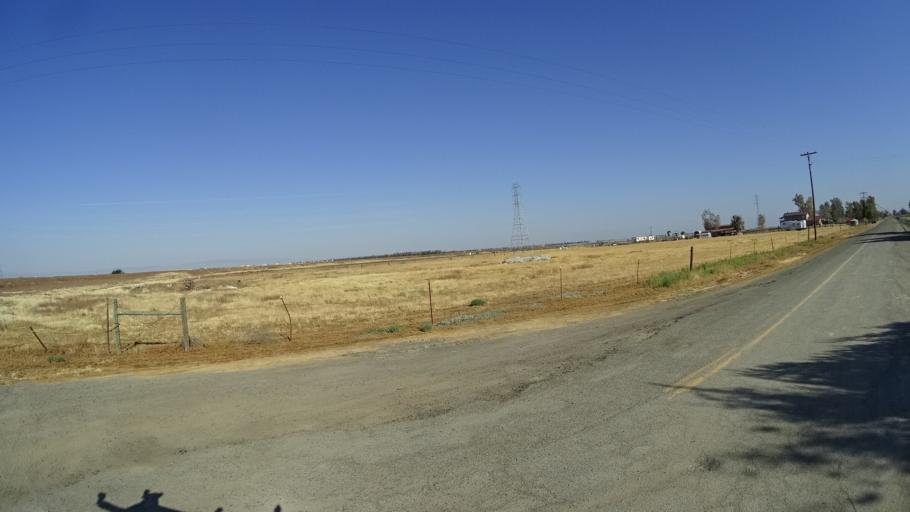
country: US
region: California
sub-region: Kings County
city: Lemoore Station
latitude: 36.3211
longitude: -119.8872
